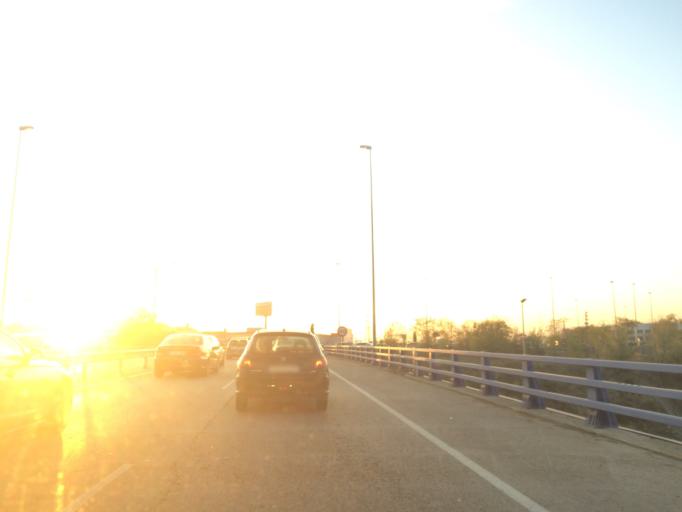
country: ES
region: Madrid
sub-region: Provincia de Madrid
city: Majadahonda
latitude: 40.4540
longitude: -3.8783
